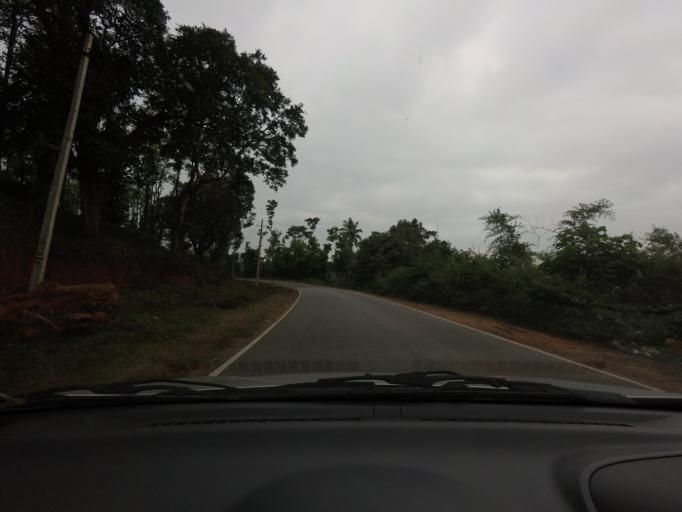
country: IN
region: Karnataka
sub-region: Hassan
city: Sakleshpur
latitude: 12.9375
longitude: 75.7624
